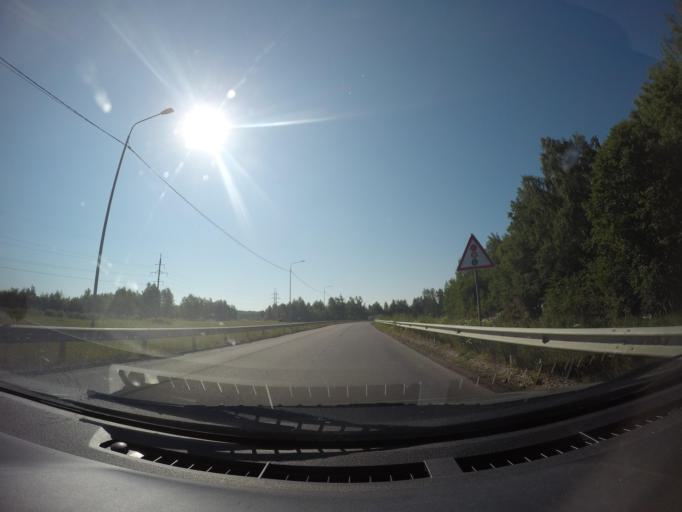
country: RU
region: Moskovskaya
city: Fryazevo
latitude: 55.7362
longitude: 38.4332
